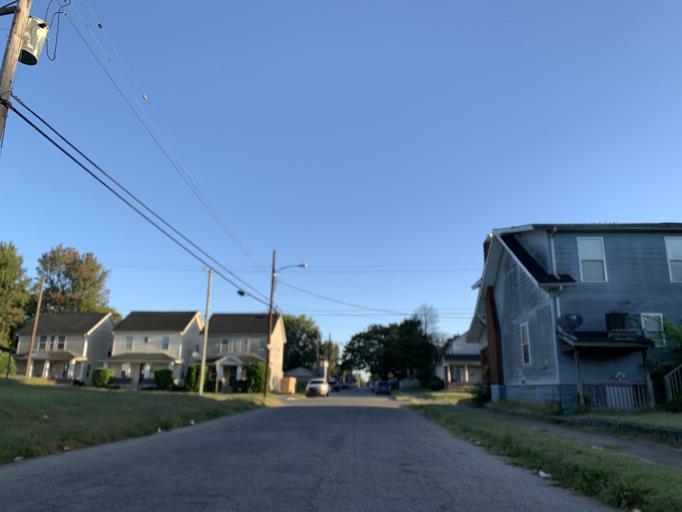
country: US
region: Kentucky
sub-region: Jefferson County
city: Louisville
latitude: 38.2373
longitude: -85.7809
